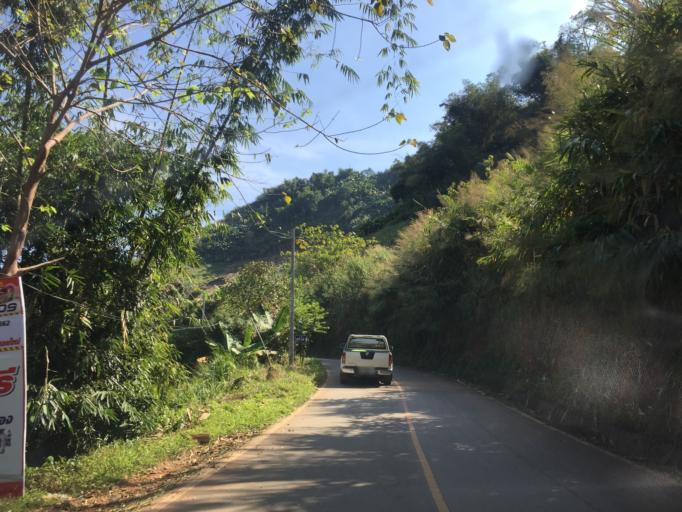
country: TH
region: Chiang Mai
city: Samoeng
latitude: 18.9424
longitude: 98.7968
